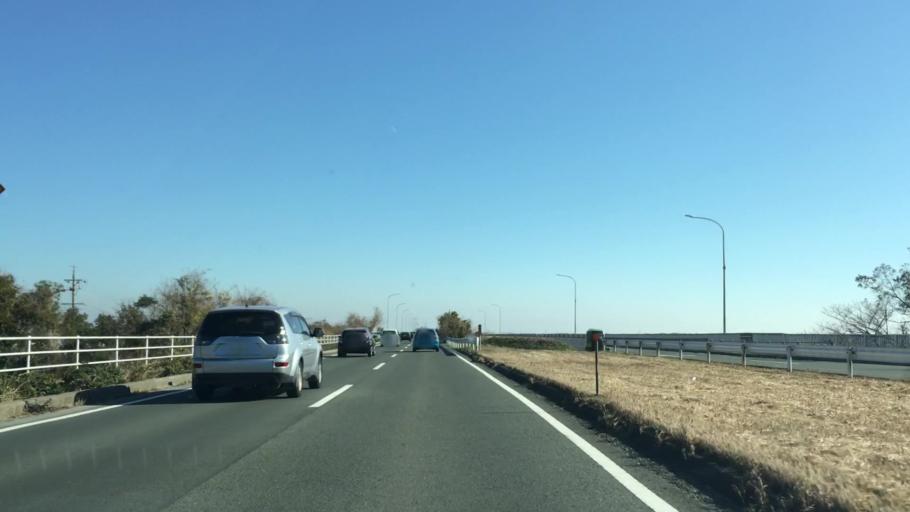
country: JP
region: Aichi
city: Tahara
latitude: 34.6942
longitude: 137.2953
